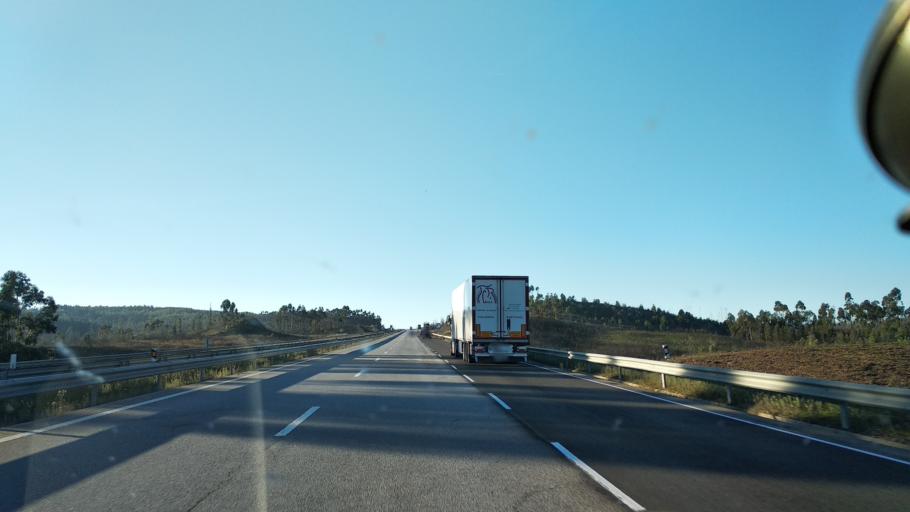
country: PT
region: Portalegre
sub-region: Gaviao
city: Gaviao
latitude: 39.5335
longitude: -7.9074
